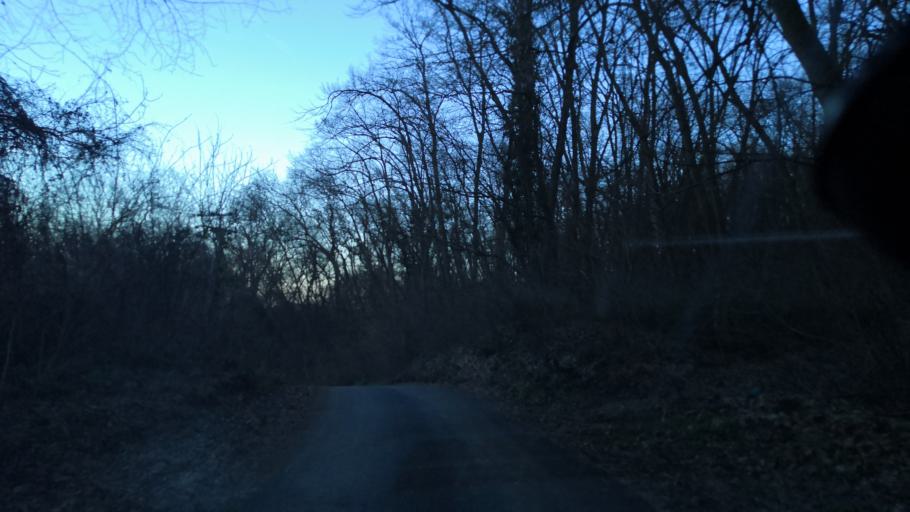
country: RS
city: Cortanovci
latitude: 45.1669
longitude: 20.0044
